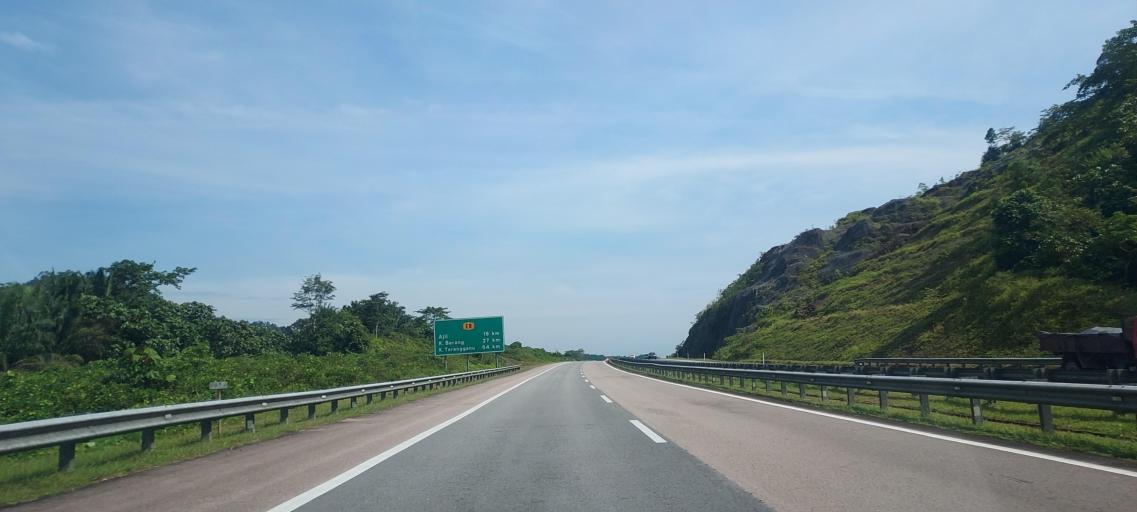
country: MY
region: Terengganu
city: Marang
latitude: 4.9505
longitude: 103.0873
